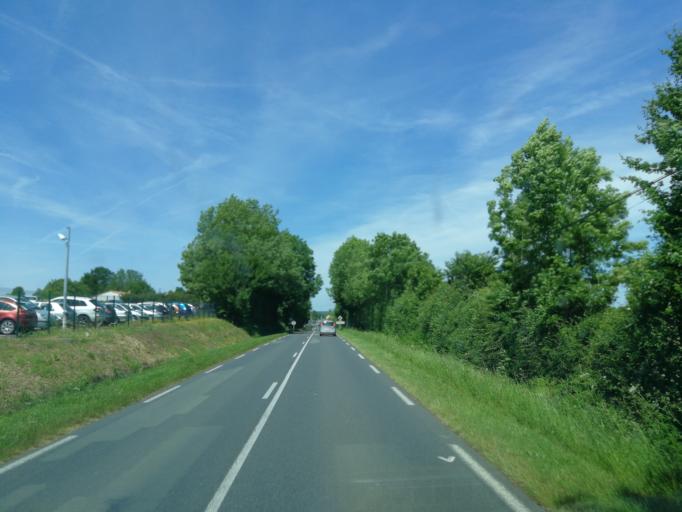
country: FR
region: Poitou-Charentes
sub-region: Departement des Deux-Sevres
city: La Foret-sur-Sevre
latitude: 46.7408
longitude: -0.6659
